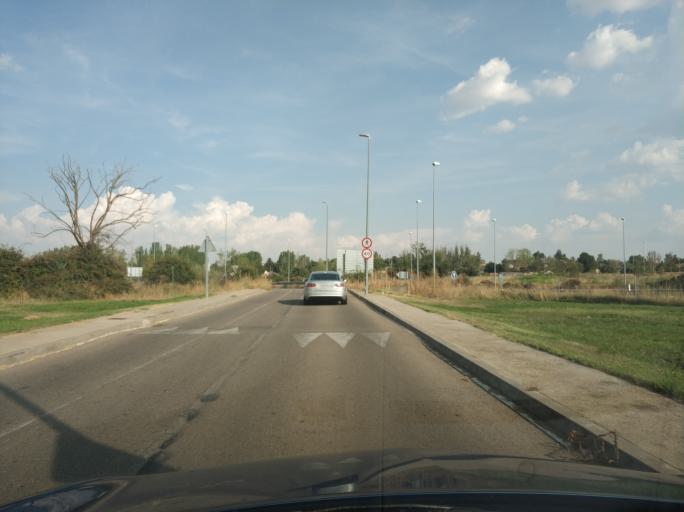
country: ES
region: Castille and Leon
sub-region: Provincia de Salamanca
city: Santa Marta de Tormes
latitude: 40.9447
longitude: -5.6376
